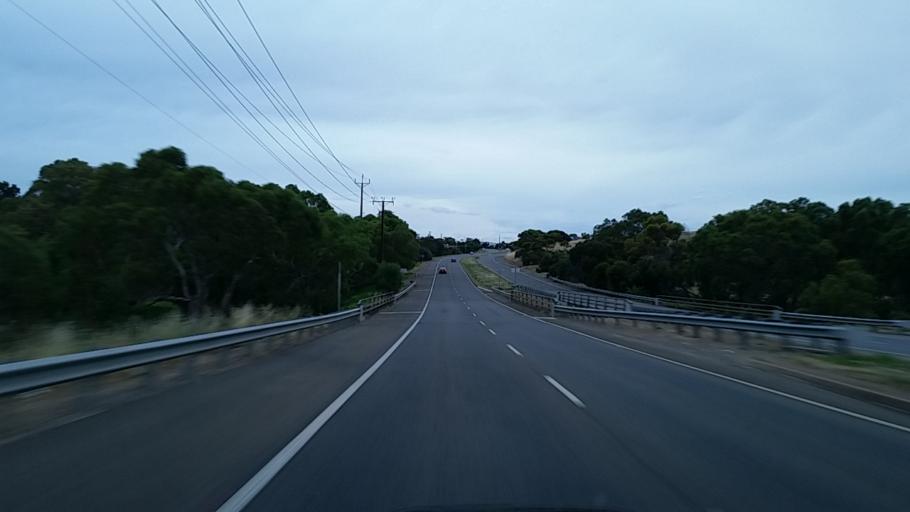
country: AU
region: South Australia
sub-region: Adelaide
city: Port Noarlunga
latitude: -35.1243
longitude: 138.4867
